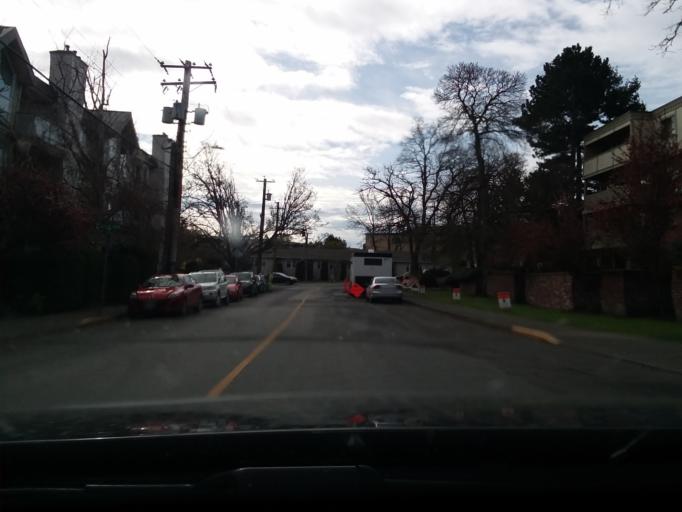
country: CA
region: British Columbia
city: Victoria
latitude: 48.4288
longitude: -123.3342
